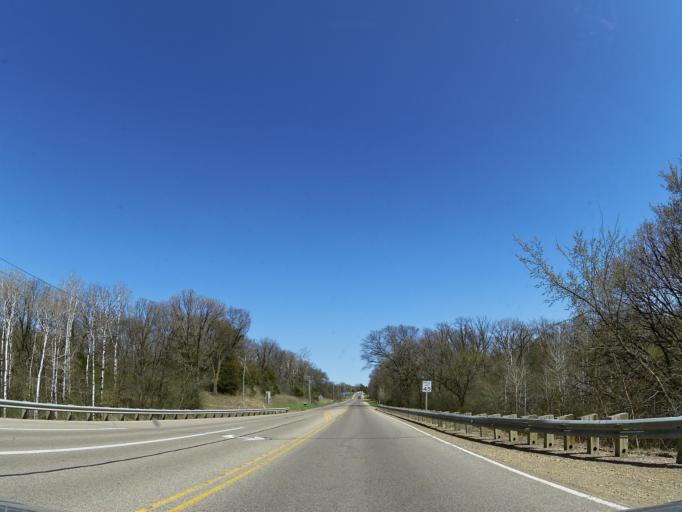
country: US
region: Wisconsin
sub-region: Saint Croix County
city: Hudson
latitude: 44.9592
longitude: -92.6898
